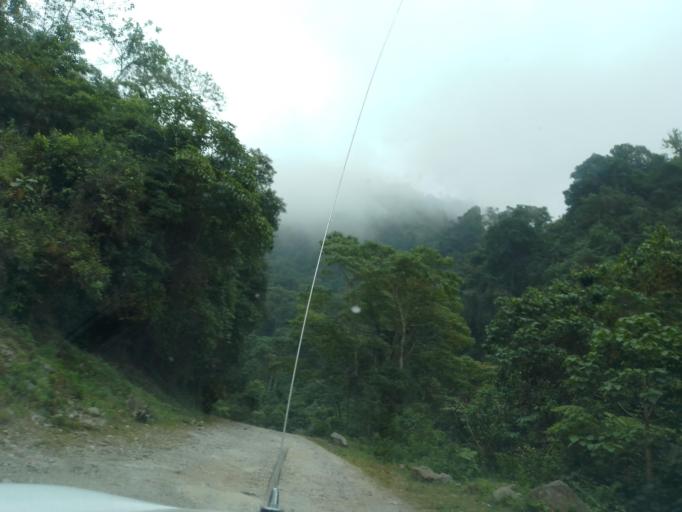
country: MX
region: Chiapas
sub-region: Union Juarez
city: Santo Domingo
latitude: 15.0929
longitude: -92.0931
